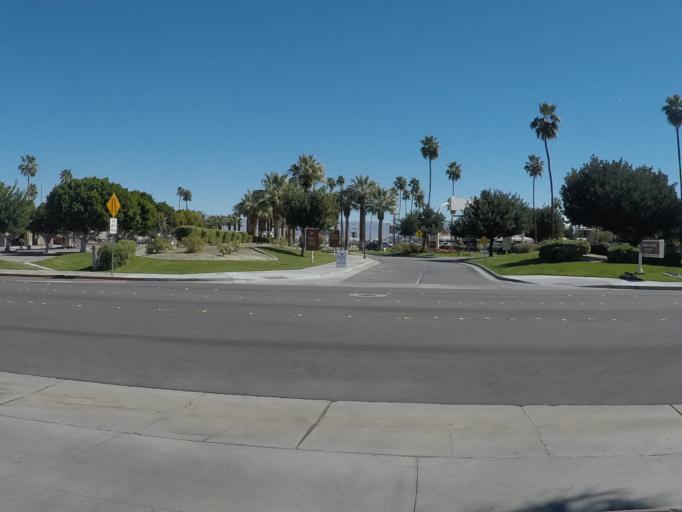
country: US
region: California
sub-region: Riverside County
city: Palm Springs
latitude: 33.8239
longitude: -116.5108
